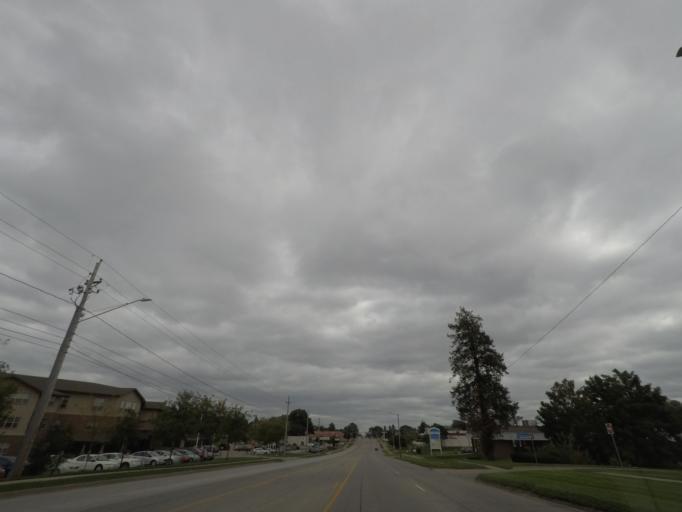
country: US
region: Iowa
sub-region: Polk County
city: Des Moines
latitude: 41.5265
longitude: -93.6217
